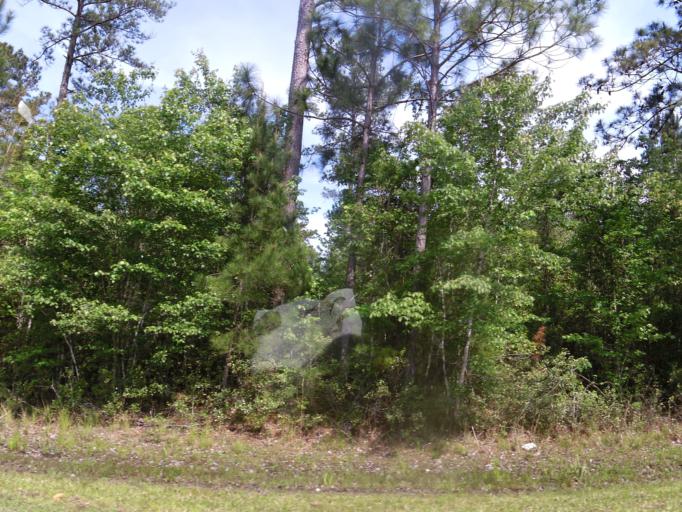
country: US
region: Georgia
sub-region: Camden County
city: Kingsland
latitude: 30.8100
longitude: -81.7514
